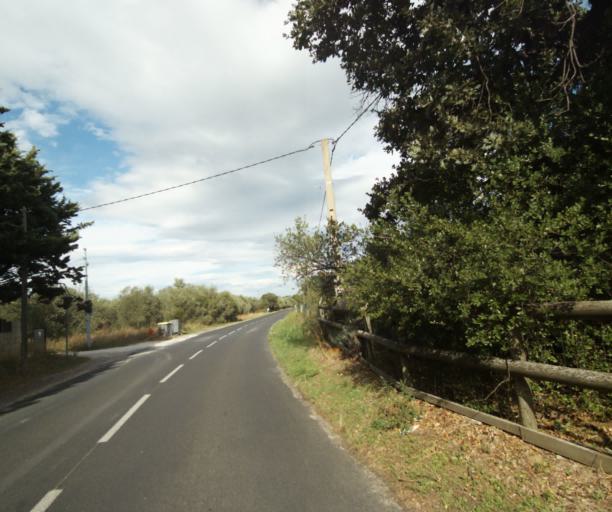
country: FR
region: Languedoc-Roussillon
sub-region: Departement des Pyrenees-Orientales
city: Argelers
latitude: 42.5394
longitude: 2.9994
